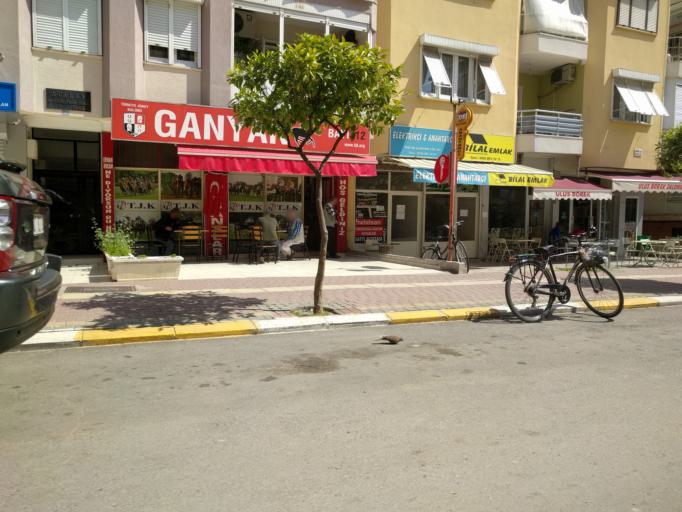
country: TR
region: Antalya
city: Antalya
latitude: 36.9105
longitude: 30.6826
